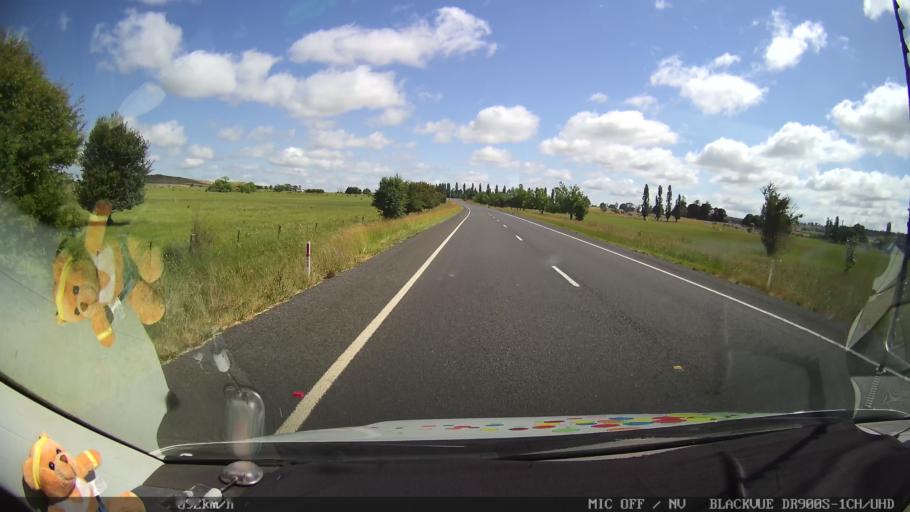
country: AU
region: New South Wales
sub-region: Glen Innes Severn
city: Glen Innes
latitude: -29.8495
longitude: 151.7378
